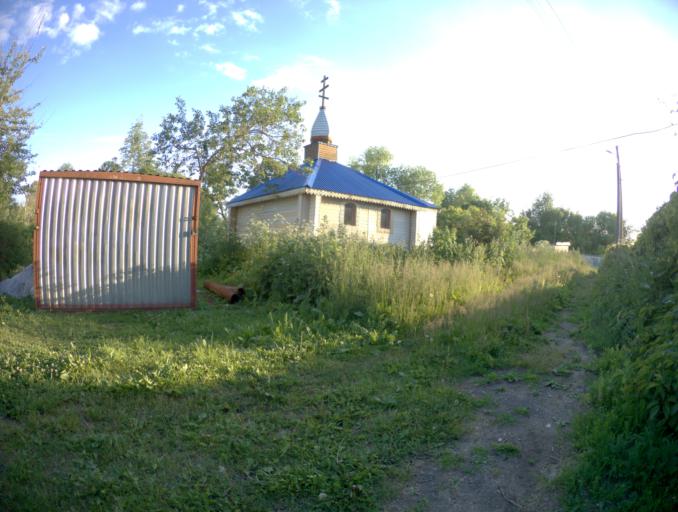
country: RU
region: Vladimir
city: Stavrovo
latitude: 56.2930
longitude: 39.9487
